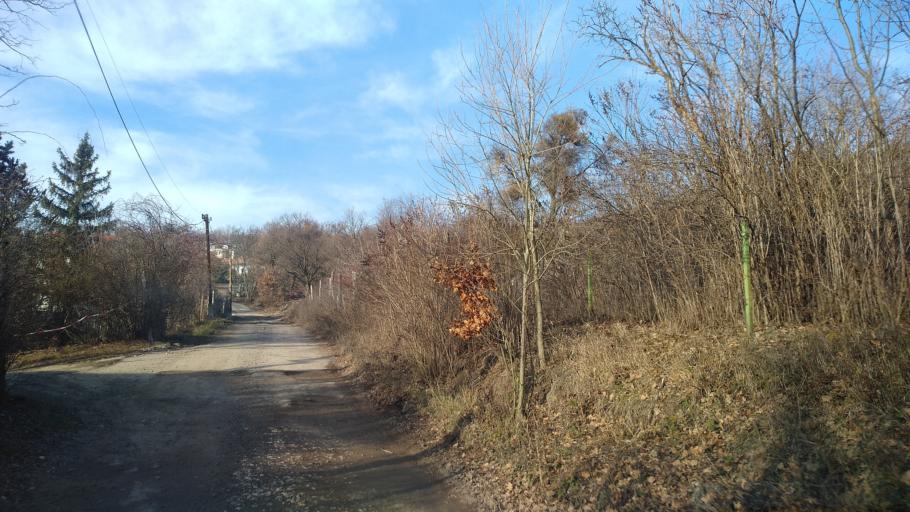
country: HU
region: Pest
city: Leanyfalu
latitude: 47.7032
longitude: 19.0492
